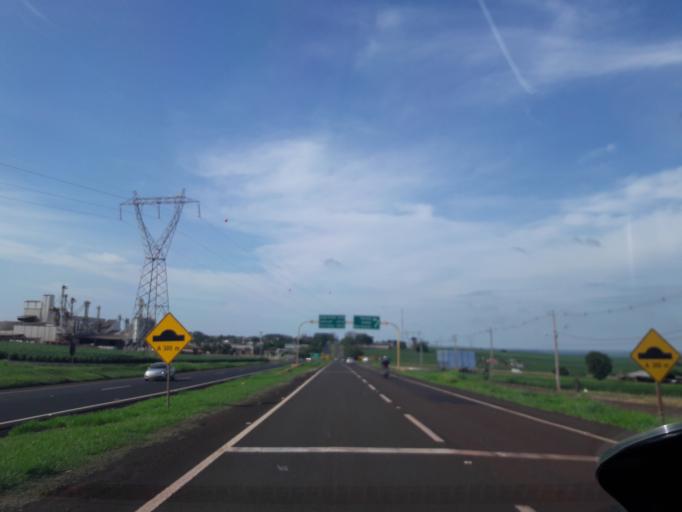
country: BR
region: Parana
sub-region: Paicandu
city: Paicandu
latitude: -23.6019
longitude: -52.0816
